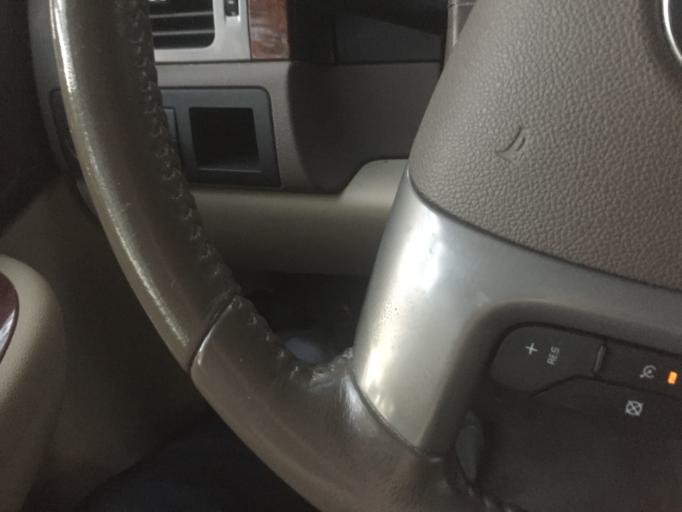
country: US
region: Louisiana
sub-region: Orleans Parish
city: New Orleans
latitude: 29.9888
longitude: -90.0957
